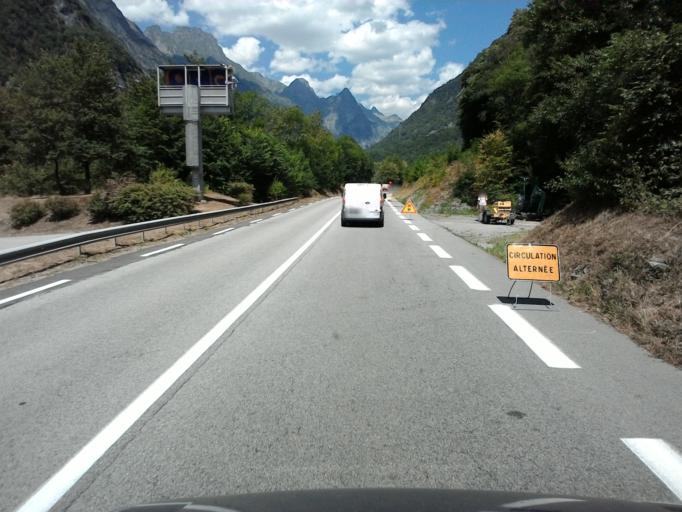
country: FR
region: Rhone-Alpes
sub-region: Departement de l'Isere
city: Livet-et-Gavet
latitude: 45.0773
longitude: 5.8862
